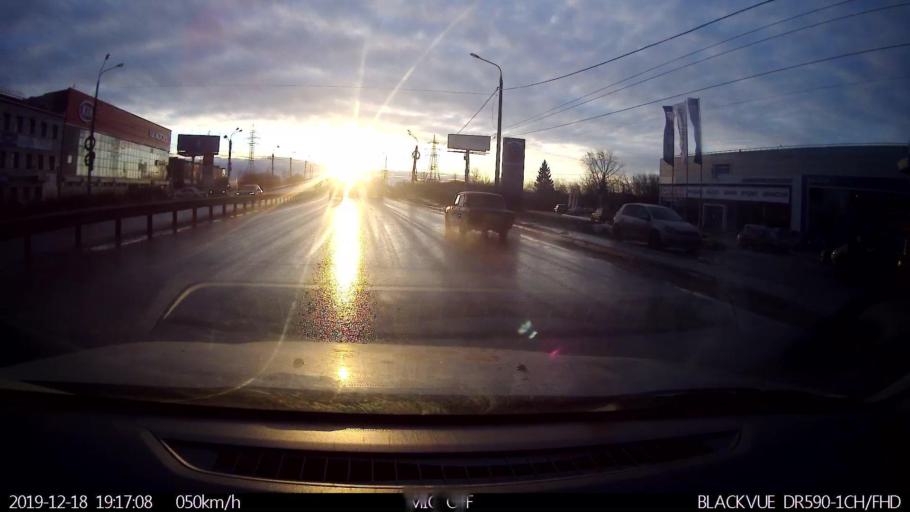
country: RU
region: Nizjnij Novgorod
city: Nizhniy Novgorod
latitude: 56.3093
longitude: 43.9005
